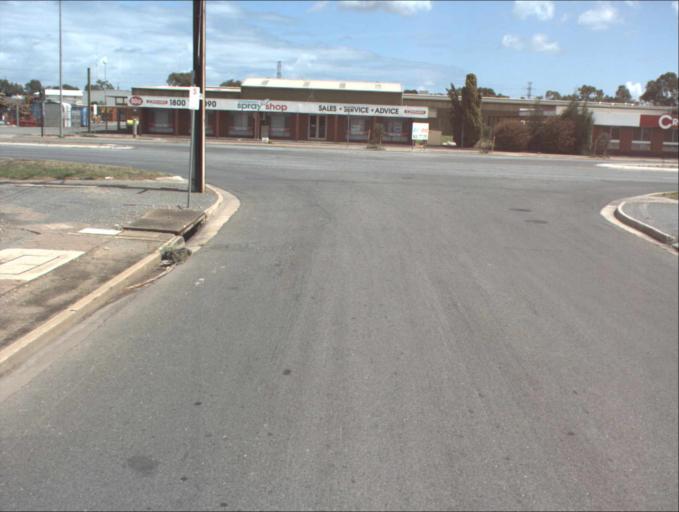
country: AU
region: South Australia
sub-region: Port Adelaide Enfield
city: Enfield
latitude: -34.8445
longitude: 138.5882
